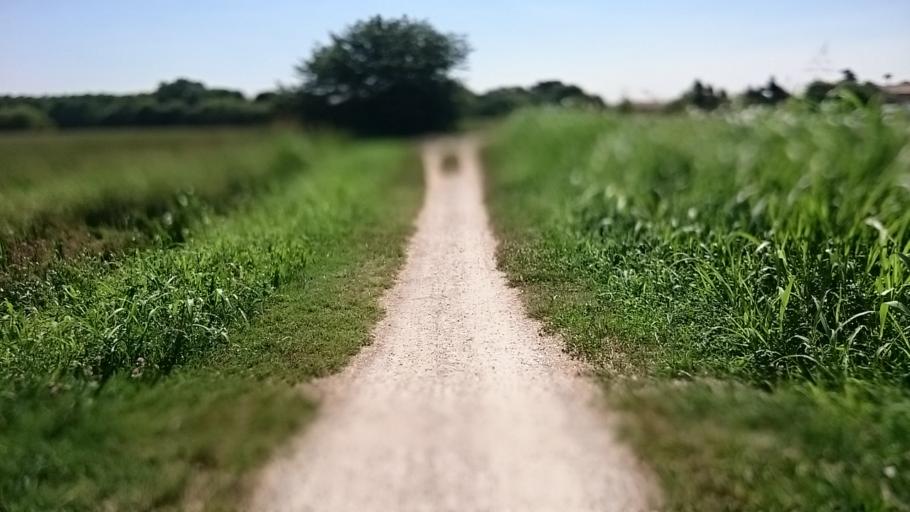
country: IT
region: Veneto
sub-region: Provincia di Padova
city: Saccolongo
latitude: 45.4060
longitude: 11.7477
